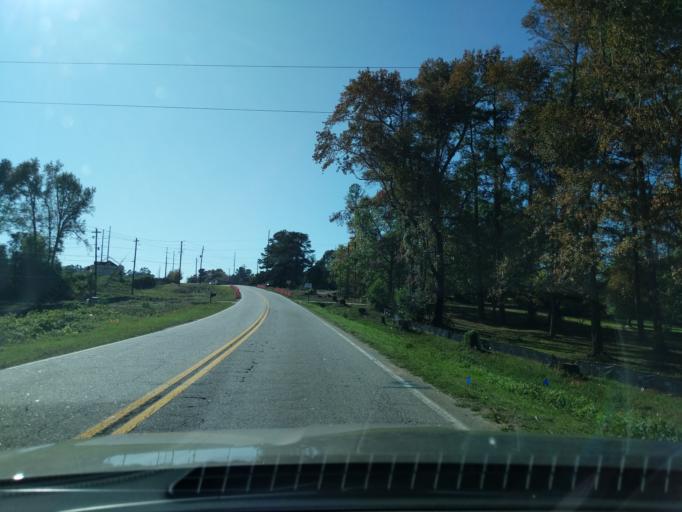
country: US
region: Georgia
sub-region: Columbia County
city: Grovetown
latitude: 33.4645
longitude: -82.1752
